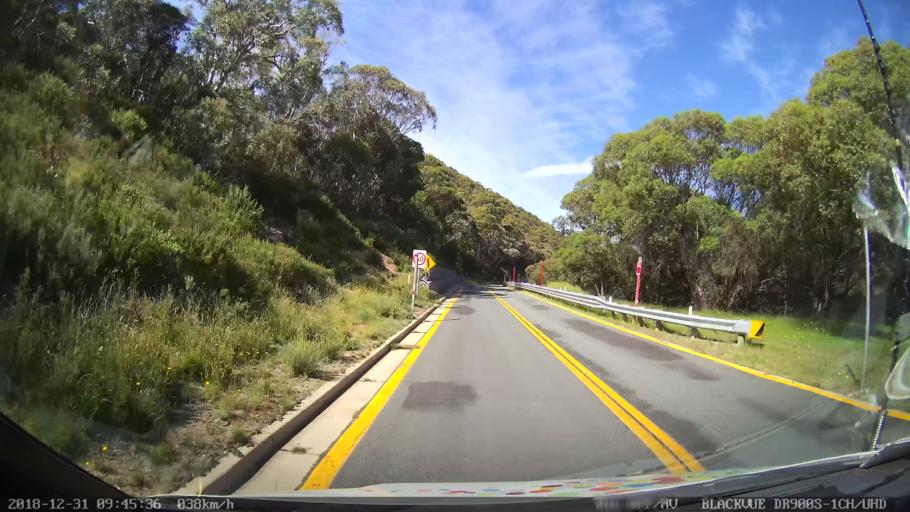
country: AU
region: New South Wales
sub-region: Snowy River
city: Jindabyne
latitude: -36.5004
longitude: 148.3164
